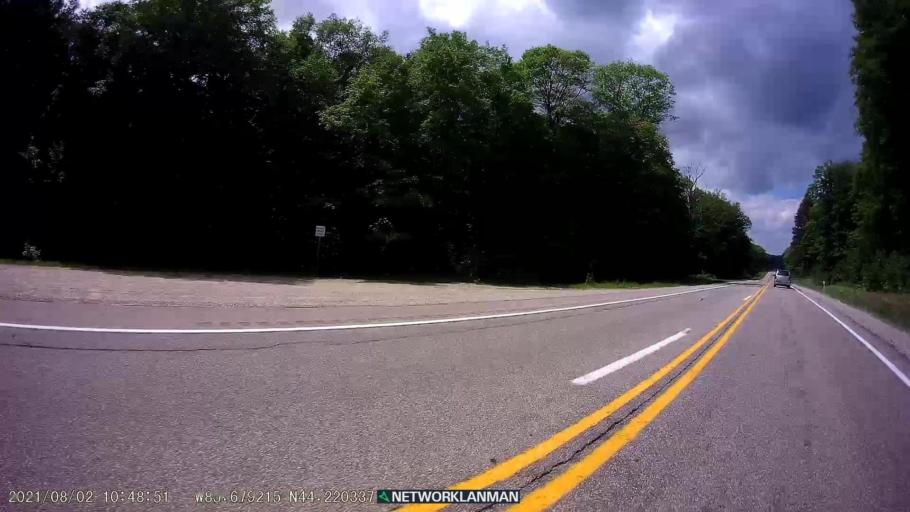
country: US
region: Michigan
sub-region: Wexford County
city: Cadillac
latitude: 44.2204
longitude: -85.6799
